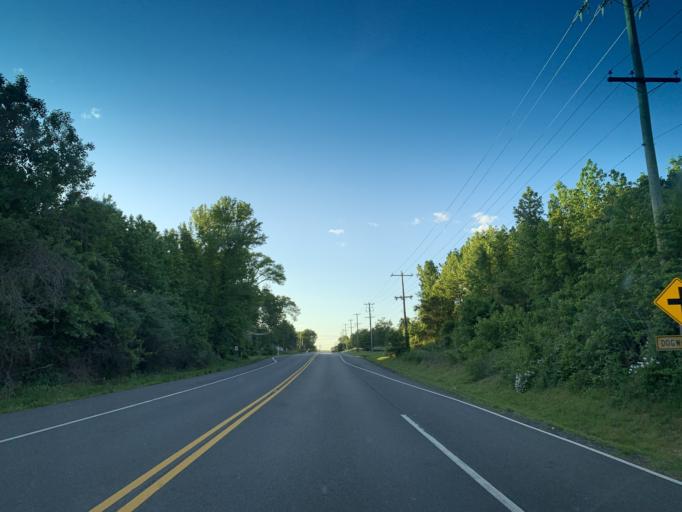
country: US
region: Maryland
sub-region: Cecil County
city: Elkton
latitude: 39.6257
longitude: -75.8404
